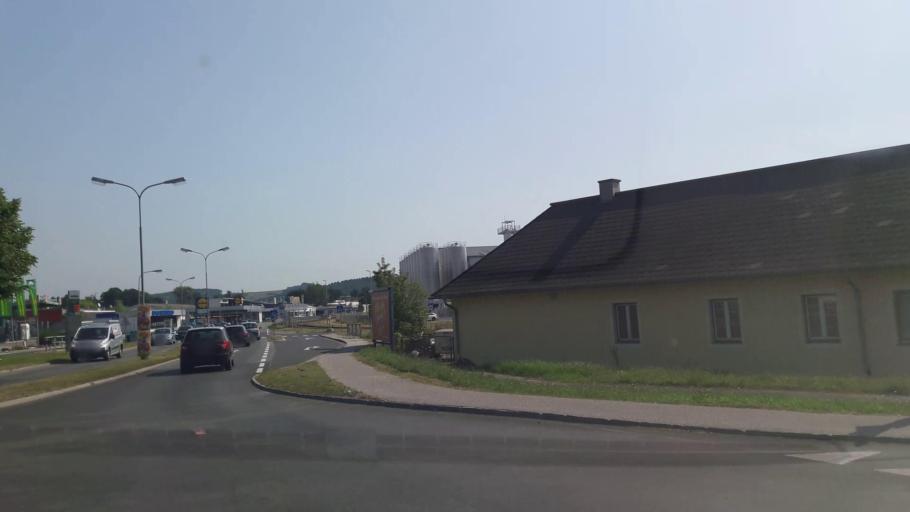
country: AT
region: Styria
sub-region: Politischer Bezirk Hartberg-Fuerstenfeld
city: Hartberg
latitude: 47.2829
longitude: 15.9858
